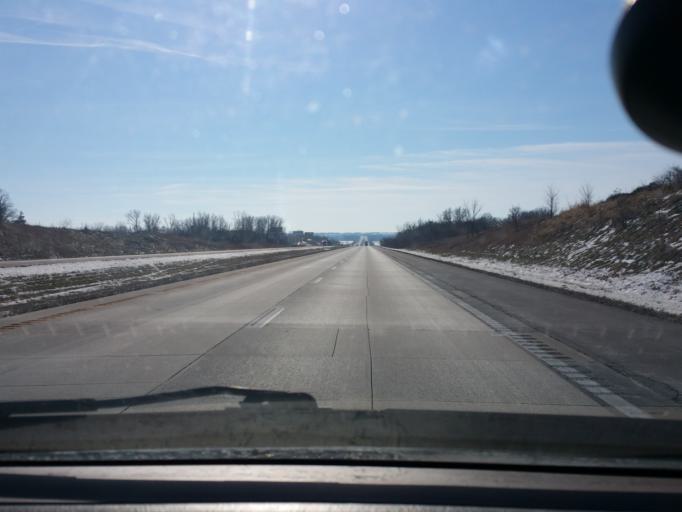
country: US
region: Missouri
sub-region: Daviess County
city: Gallatin
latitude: 40.0644
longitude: -94.0942
